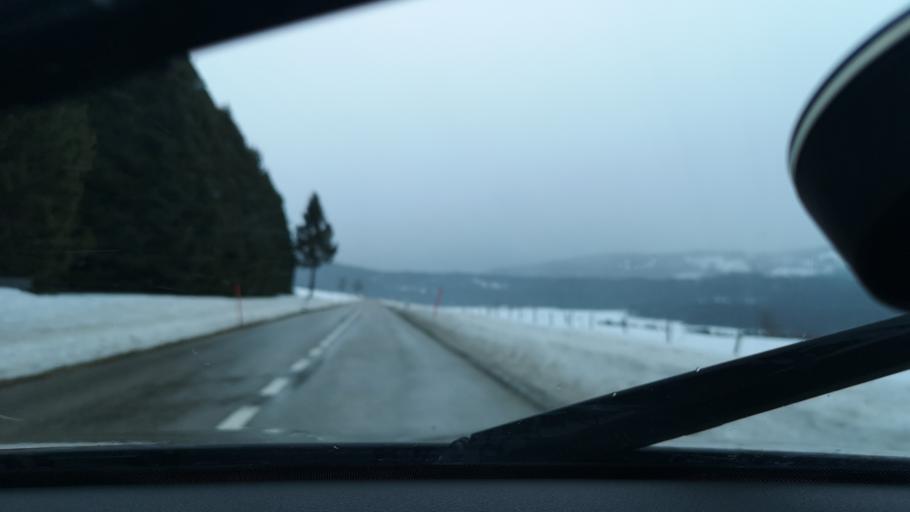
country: FR
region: Franche-Comte
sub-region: Departement du Doubs
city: Les Fourgs
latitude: 46.8195
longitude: 6.4418
